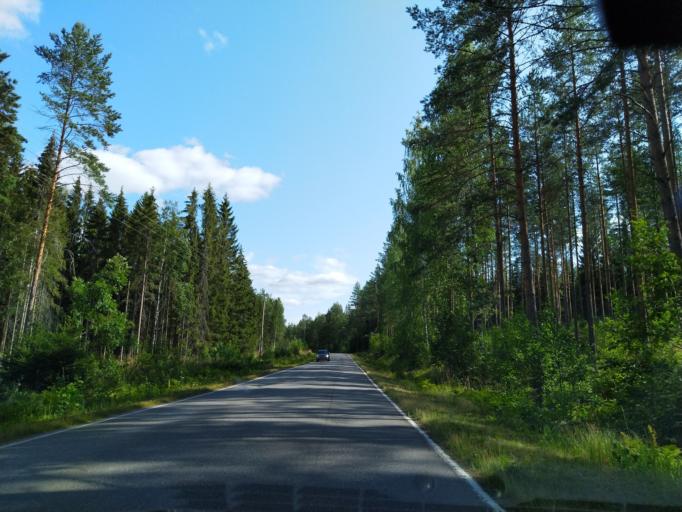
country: FI
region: Uusimaa
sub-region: Helsinki
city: Karkkila
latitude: 60.6609
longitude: 24.1988
